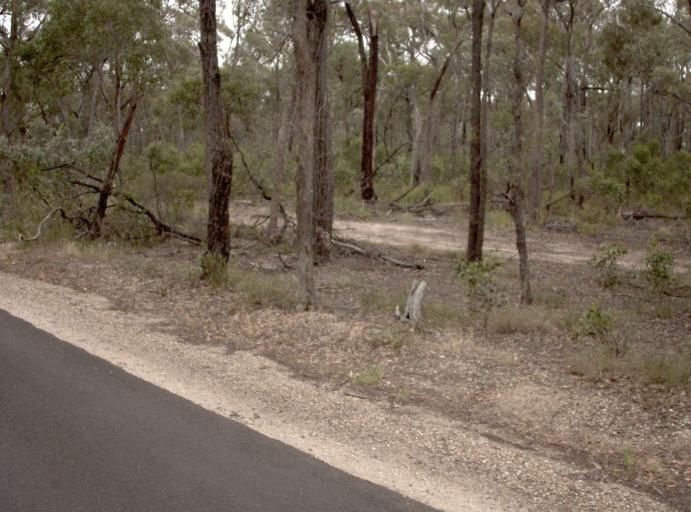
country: AU
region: Victoria
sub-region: Wellington
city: Heyfield
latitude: -37.9537
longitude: 146.7696
